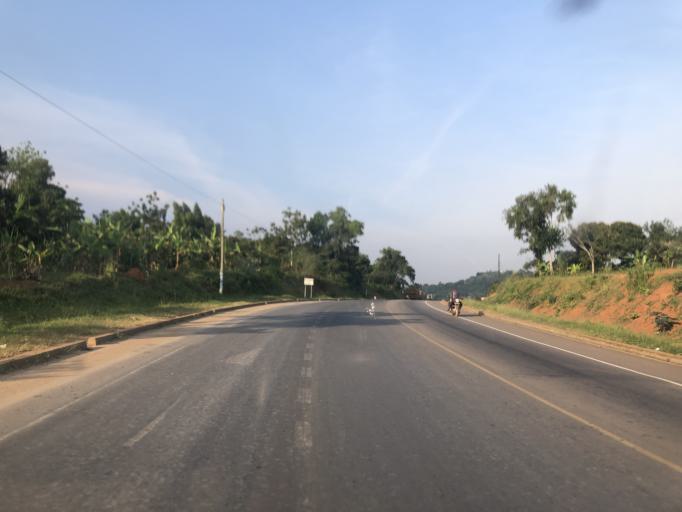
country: UG
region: Central Region
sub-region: Mpigi District
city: Mpigi
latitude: 0.1716
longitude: 32.2617
